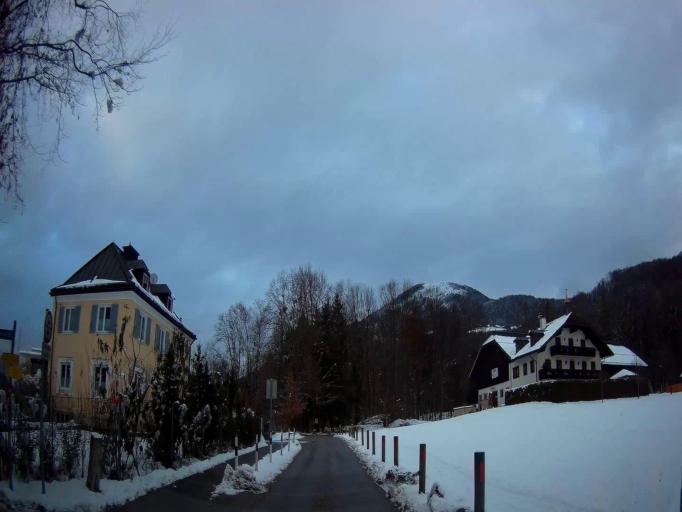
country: AT
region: Salzburg
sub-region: Politischer Bezirk Salzburg-Umgebung
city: Elsbethen
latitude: 47.7819
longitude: 13.0899
